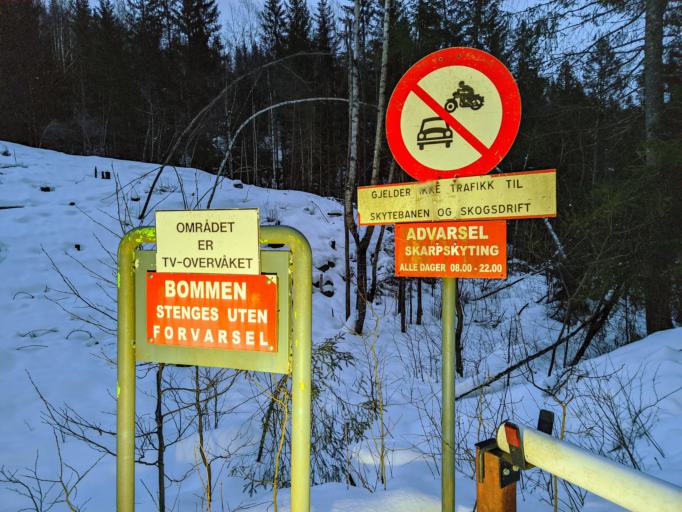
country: NO
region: Akershus
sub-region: Gjerdrum
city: Ask
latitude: 60.0638
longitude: 11.0108
